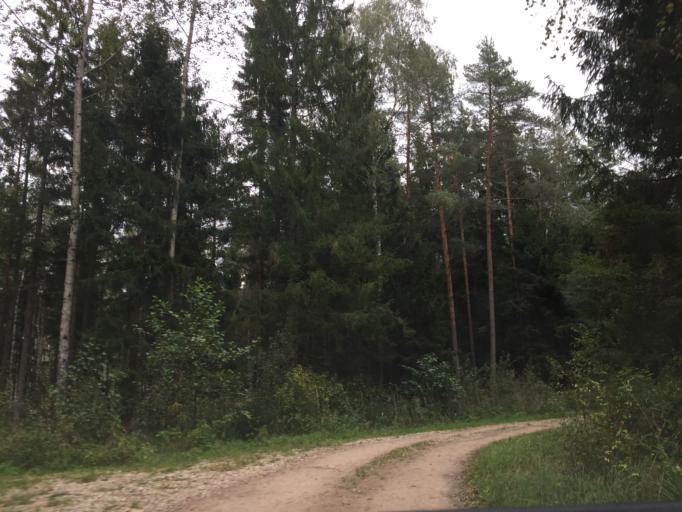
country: LV
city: Tireli
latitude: 56.8917
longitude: 23.5411
